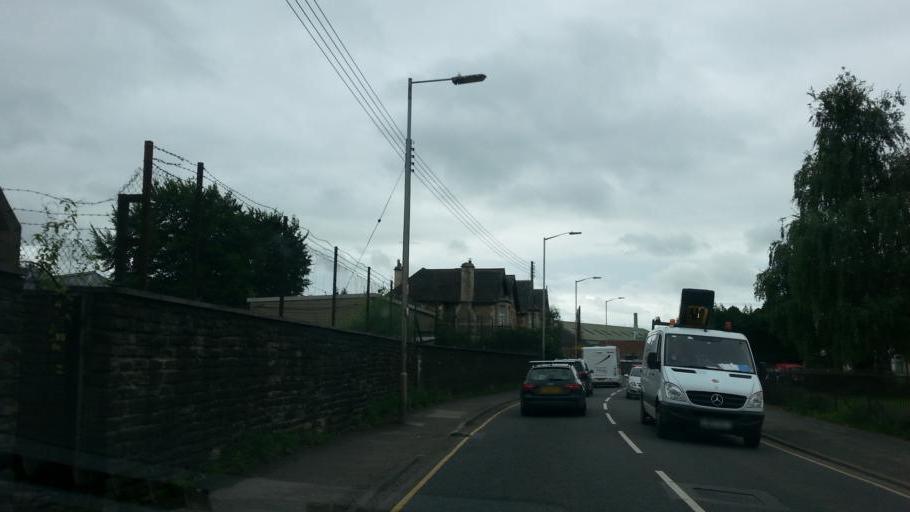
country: GB
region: England
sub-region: Wiltshire
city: Melksham
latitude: 51.3803
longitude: -2.1420
